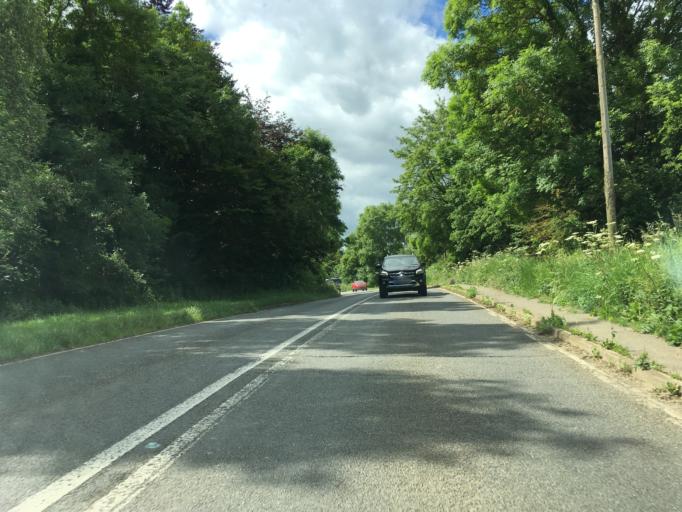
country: GB
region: England
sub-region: Oxfordshire
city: Bloxham
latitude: 52.0322
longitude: -1.3658
